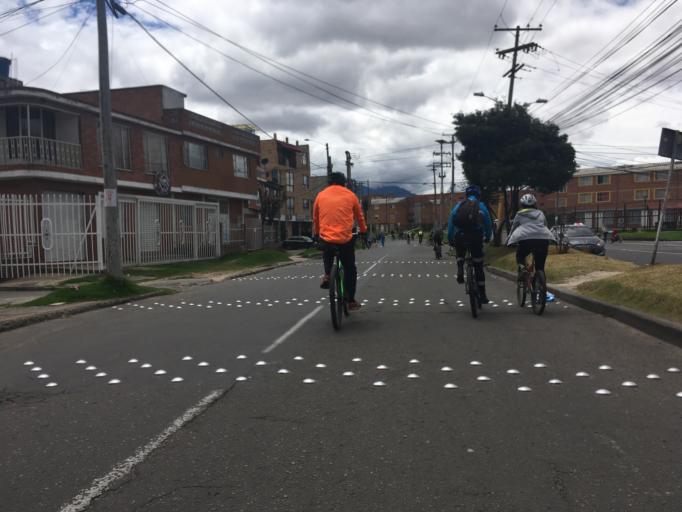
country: CO
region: Bogota D.C.
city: Bogota
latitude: 4.6095
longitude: -74.1492
